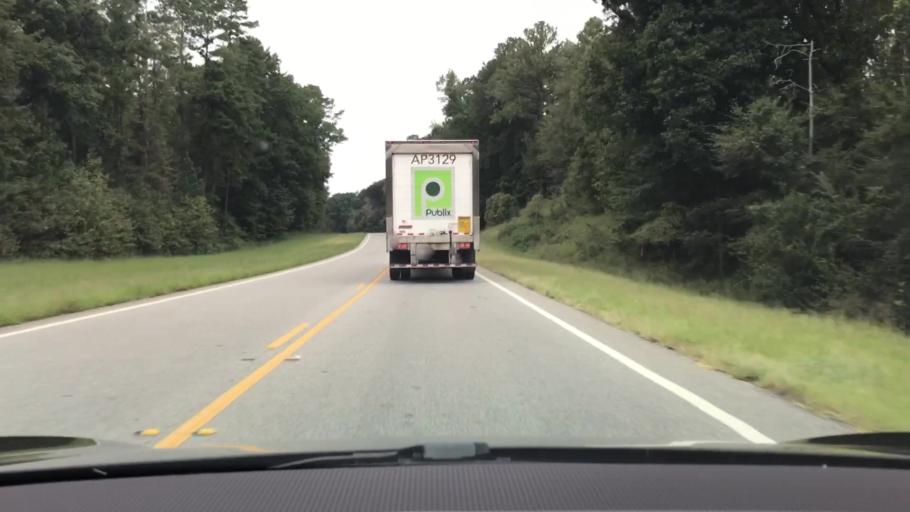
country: US
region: Georgia
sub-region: Greene County
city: Greensboro
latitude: 33.6931
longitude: -83.2766
